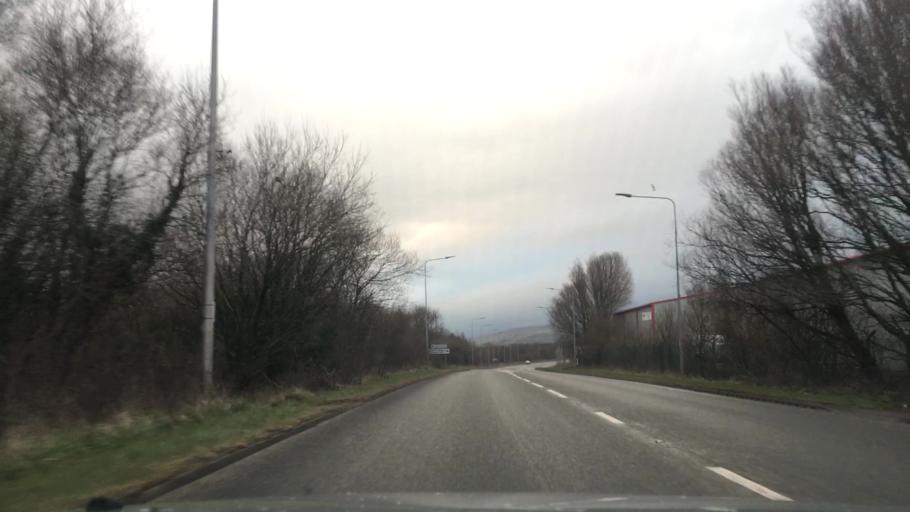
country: GB
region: England
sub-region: Cumbria
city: Askam in Furness
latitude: 54.1502
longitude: -3.2280
